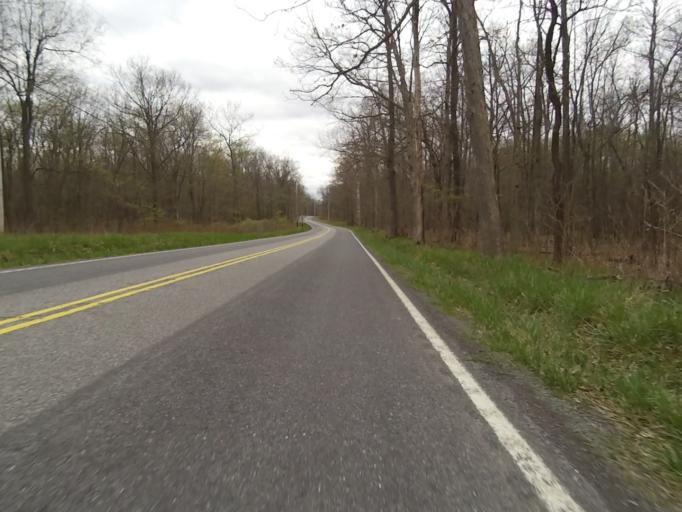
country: US
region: Pennsylvania
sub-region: Clearfield County
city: Troy
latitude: 40.9043
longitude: -78.1253
